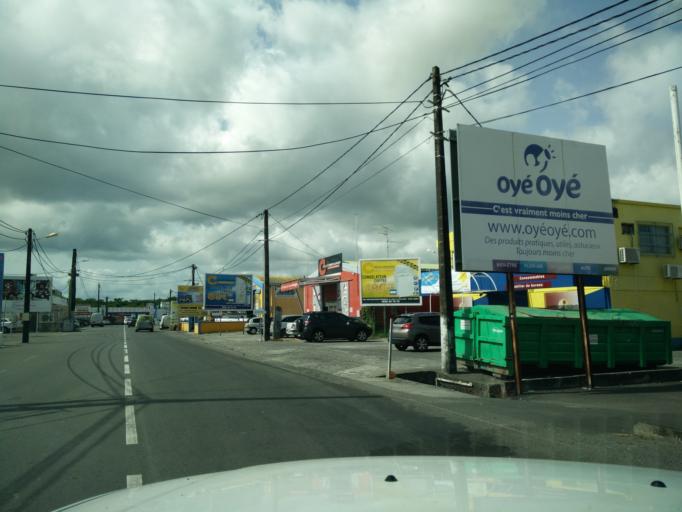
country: GP
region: Guadeloupe
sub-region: Guadeloupe
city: Pointe-a-Pitre
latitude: 16.2438
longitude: -61.5599
